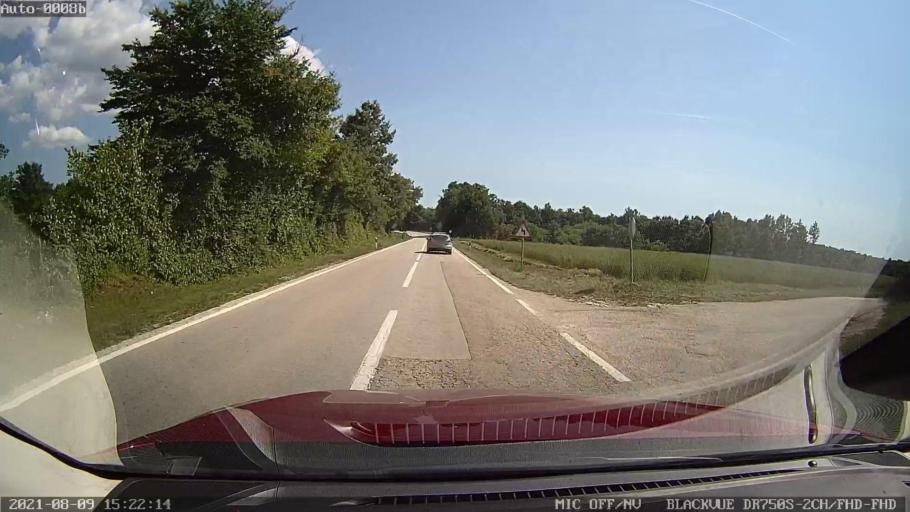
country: HR
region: Istarska
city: Pazin
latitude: 45.1927
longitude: 13.9003
